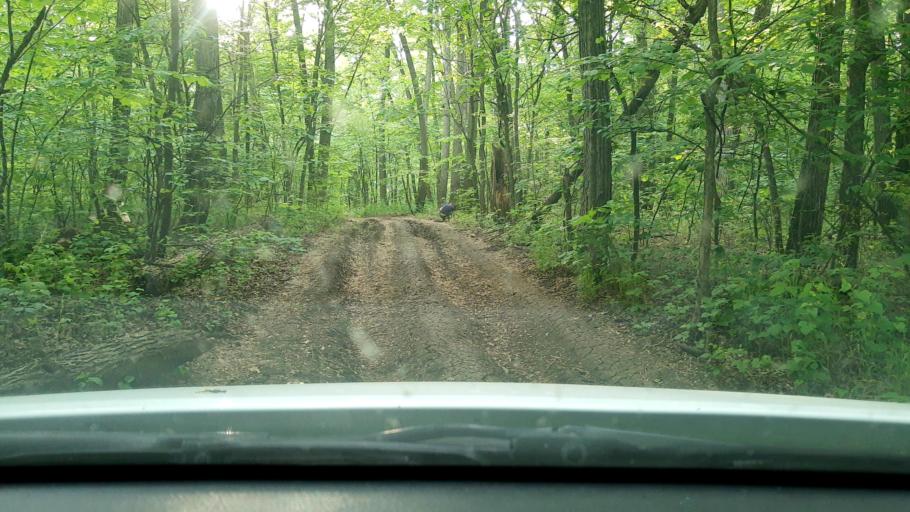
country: RU
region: Bashkortostan
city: Ufa
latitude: 54.6580
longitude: 55.8774
